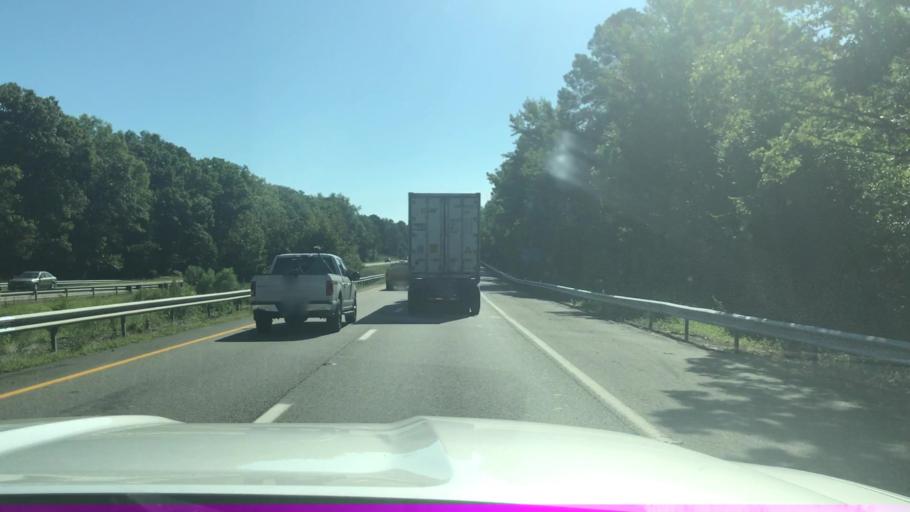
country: US
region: Virginia
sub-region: Henrico County
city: Sandston
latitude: 37.5287
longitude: -77.3076
